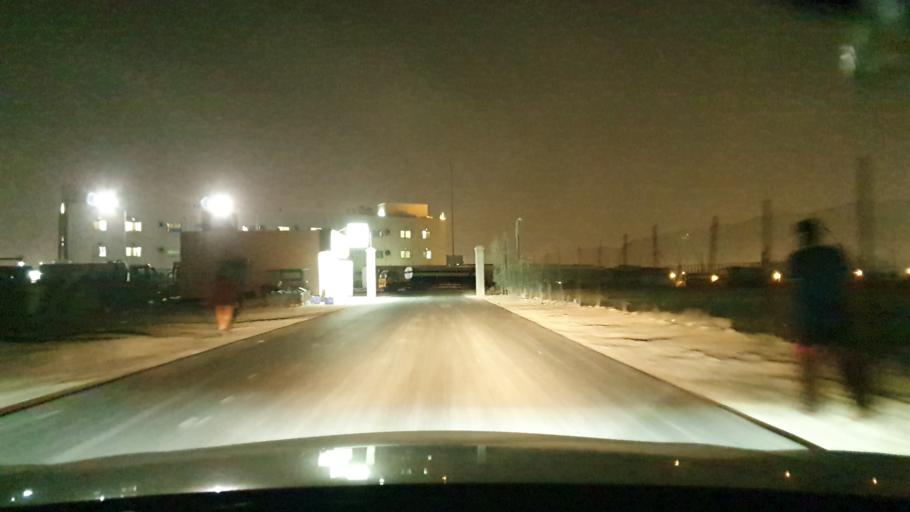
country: BH
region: Northern
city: Sitrah
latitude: 26.0973
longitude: 50.6156
